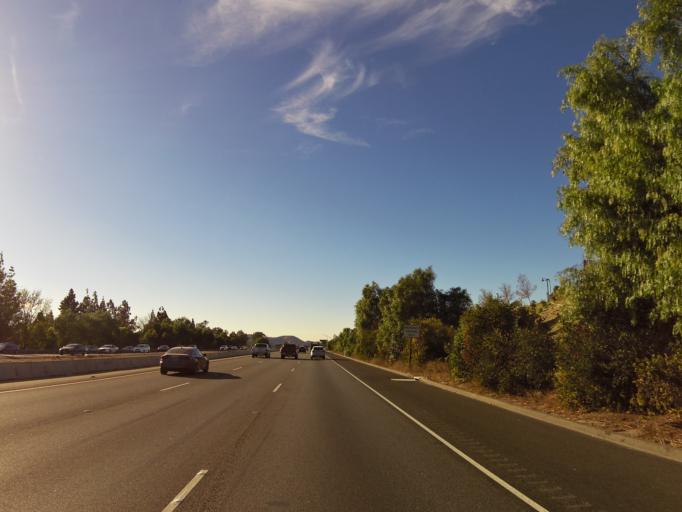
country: US
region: California
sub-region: Ventura County
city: Simi Valley
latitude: 34.2824
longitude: -118.7697
